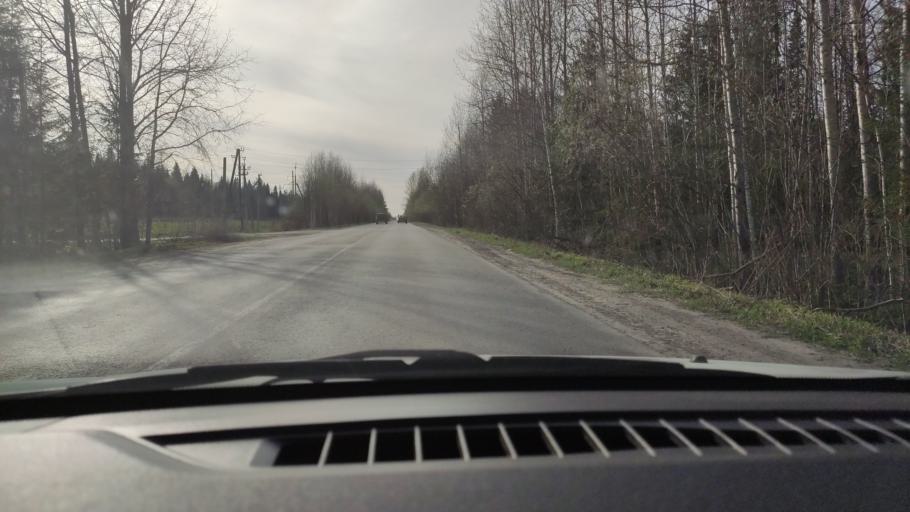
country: RU
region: Perm
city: Ferma
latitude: 57.9378
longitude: 56.4591
